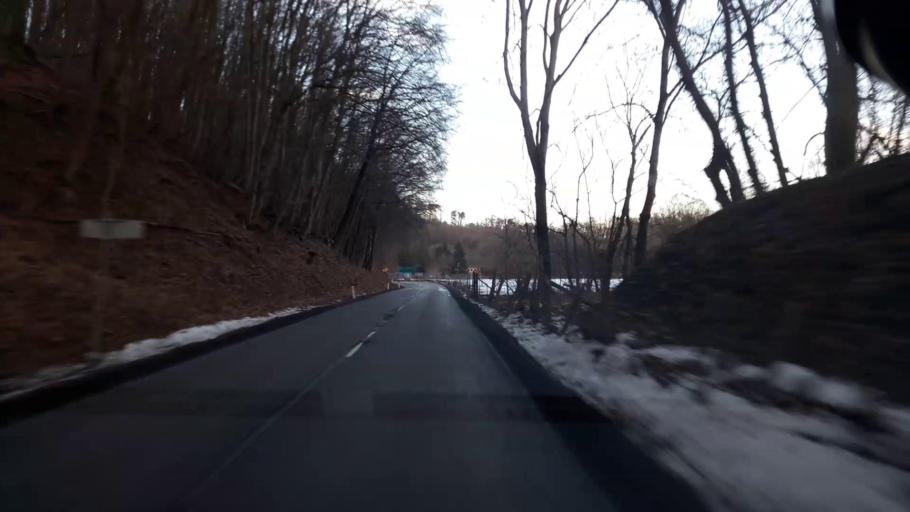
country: AT
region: Lower Austria
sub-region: Politischer Bezirk Wien-Umgebung
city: Klosterneuburg
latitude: 48.2756
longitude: 16.2759
